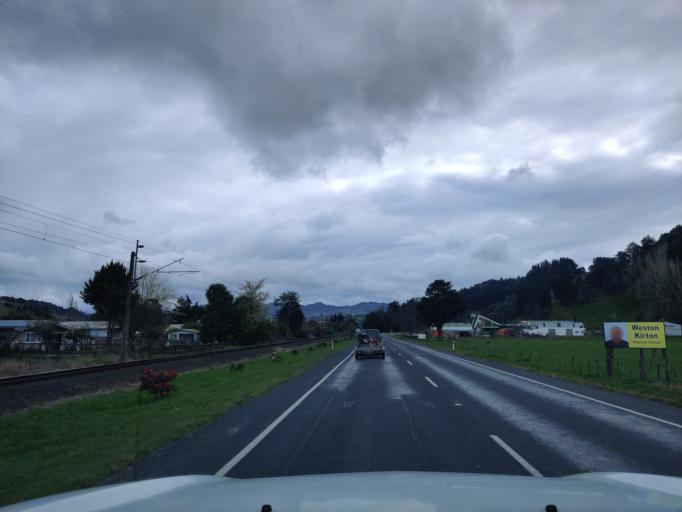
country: NZ
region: Waikato
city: Turangi
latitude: -38.8816
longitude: 175.2844
